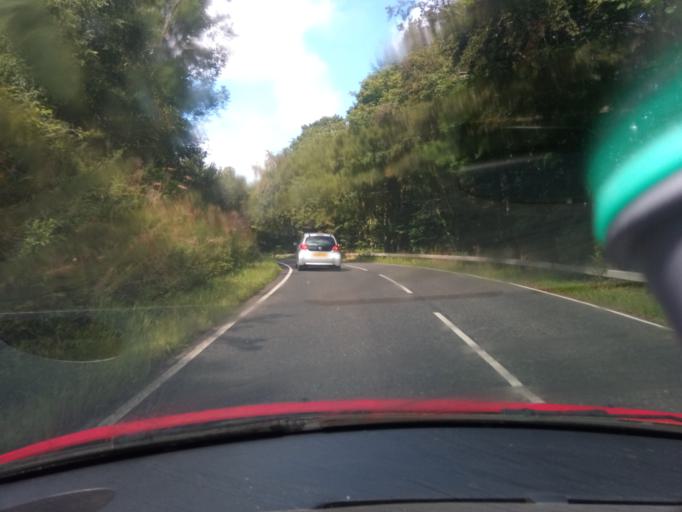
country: GB
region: Scotland
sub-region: The Scottish Borders
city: Jedburgh
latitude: 55.5716
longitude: -2.5391
